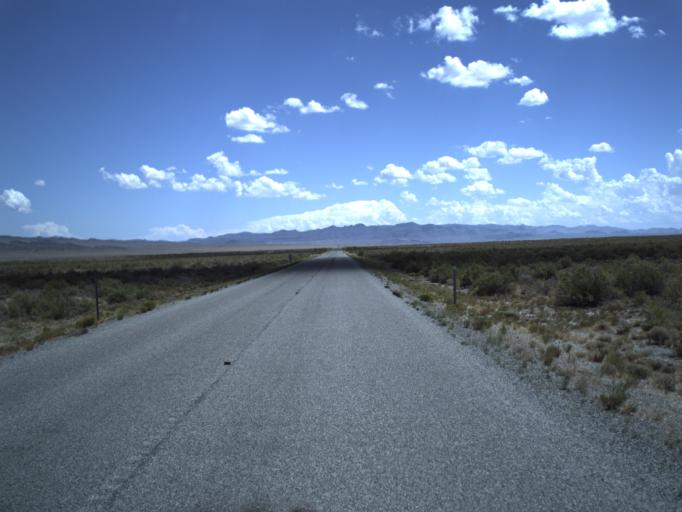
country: US
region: Nevada
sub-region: White Pine County
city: McGill
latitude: 39.0517
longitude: -113.9784
